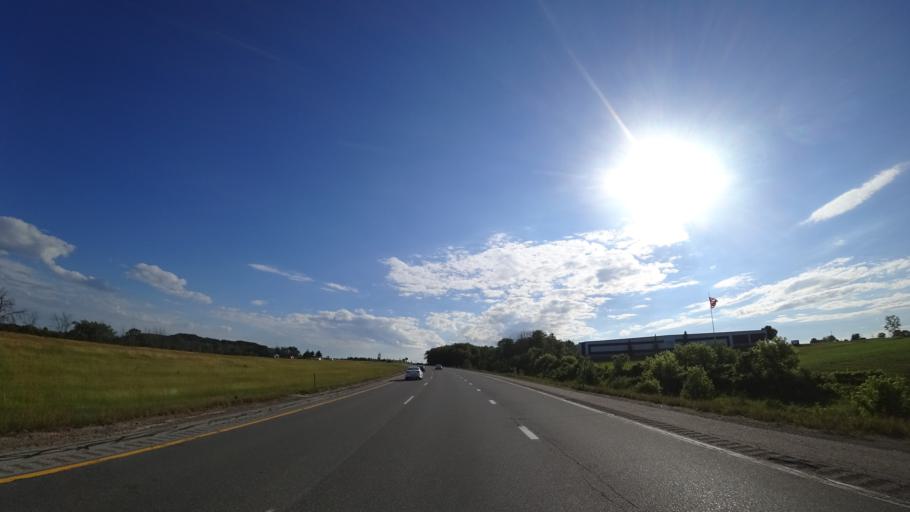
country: US
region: Michigan
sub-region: Ottawa County
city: Zeeland
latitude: 42.8163
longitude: -85.9755
